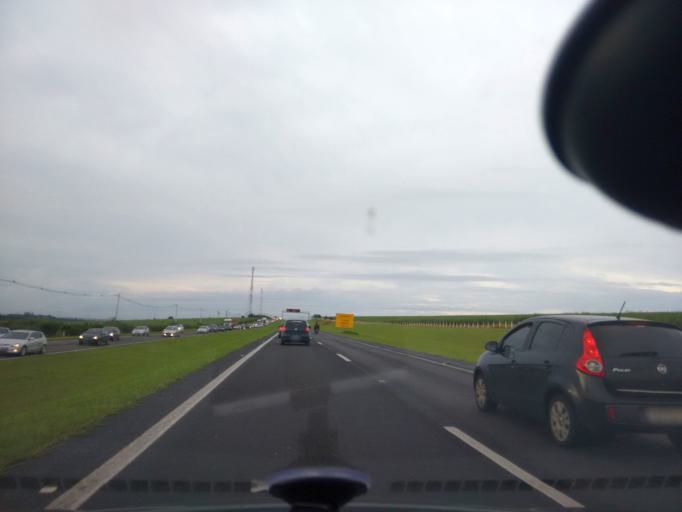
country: BR
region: Sao Paulo
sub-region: Itirapina
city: Itirapina
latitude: -22.1986
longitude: -47.7739
